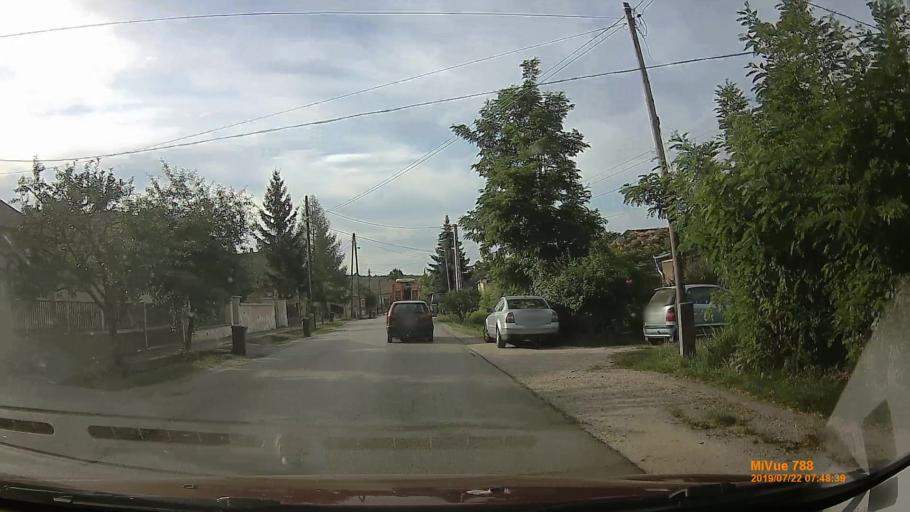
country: HU
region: Veszprem
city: Ajka
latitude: 47.0737
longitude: 17.5490
